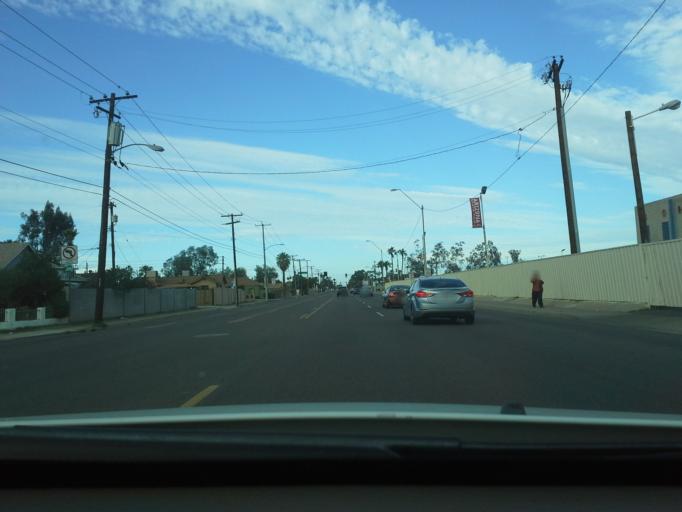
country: US
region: Arizona
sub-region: Maricopa County
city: Phoenix
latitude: 33.4690
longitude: -112.0999
